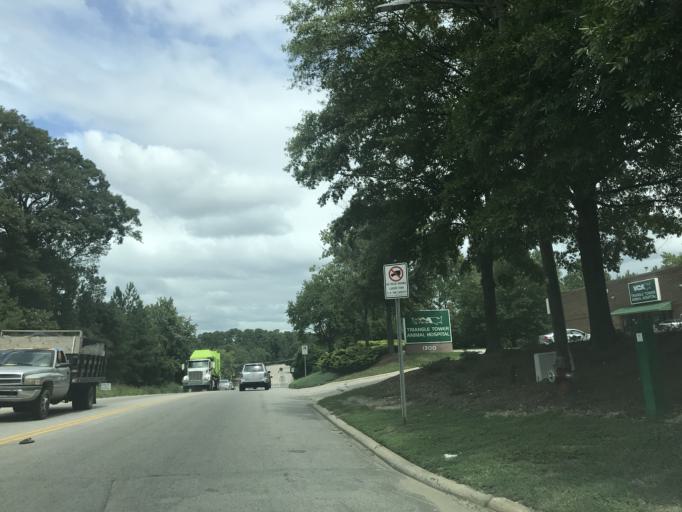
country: US
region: North Carolina
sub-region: Wake County
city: Raleigh
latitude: 35.7970
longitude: -78.5686
